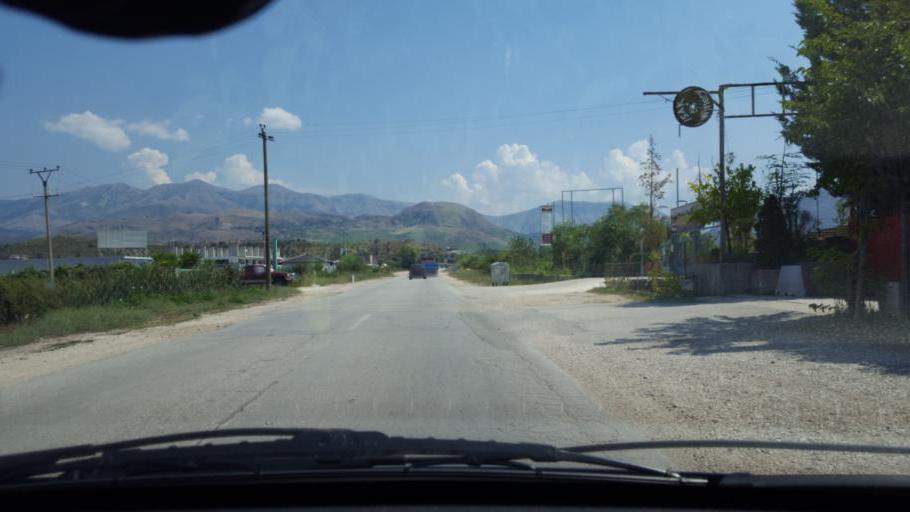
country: AL
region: Vlore
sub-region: Rrethi i Delvines
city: Finiq
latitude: 39.8942
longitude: 20.0694
